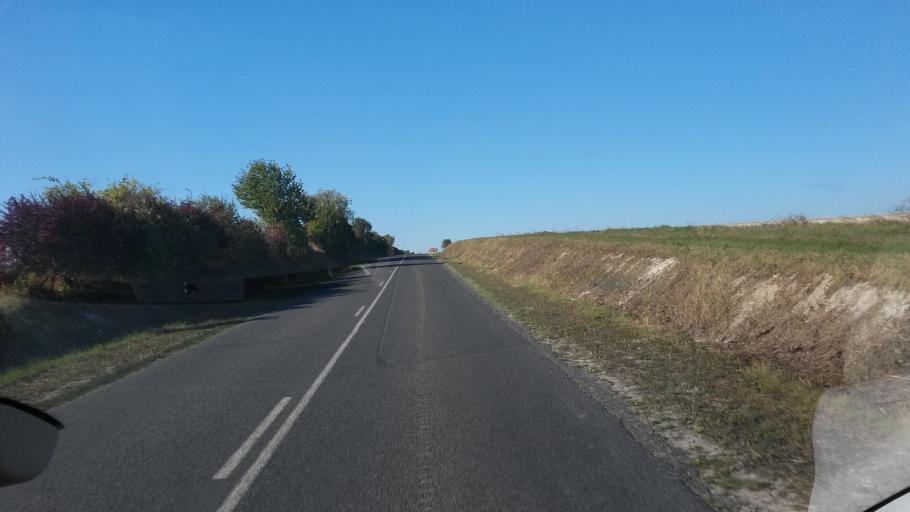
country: FR
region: Champagne-Ardenne
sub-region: Departement de la Marne
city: Connantre
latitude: 48.7648
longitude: 3.8713
